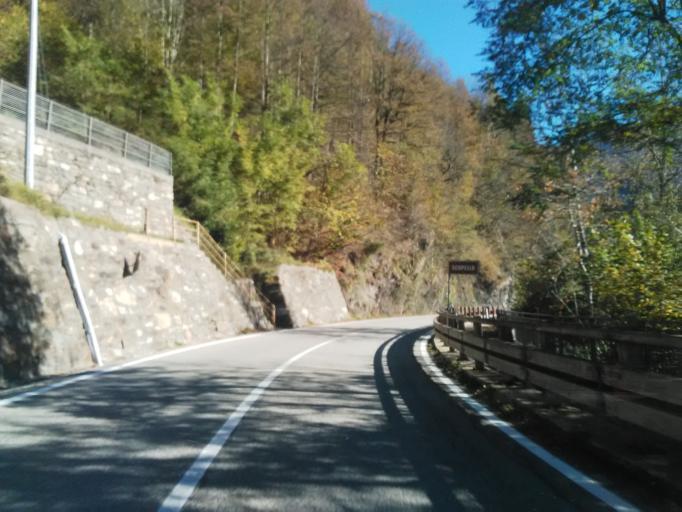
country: IT
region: Piedmont
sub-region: Provincia di Vercelli
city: Pila
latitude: 45.7704
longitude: 8.0857
